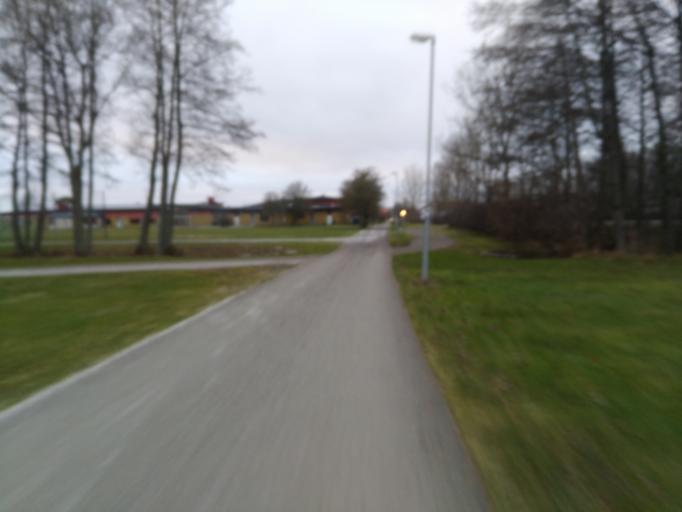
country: SE
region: Vaestra Goetaland
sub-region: Lidkopings Kommun
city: Lidkoping
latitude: 58.4930
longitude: 13.1759
